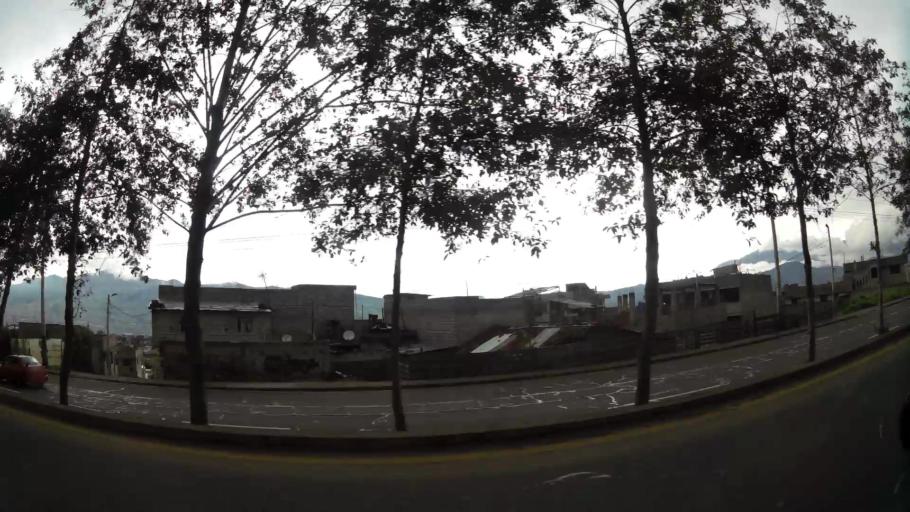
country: EC
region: Pichincha
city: Quito
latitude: -0.2942
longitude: -78.5199
